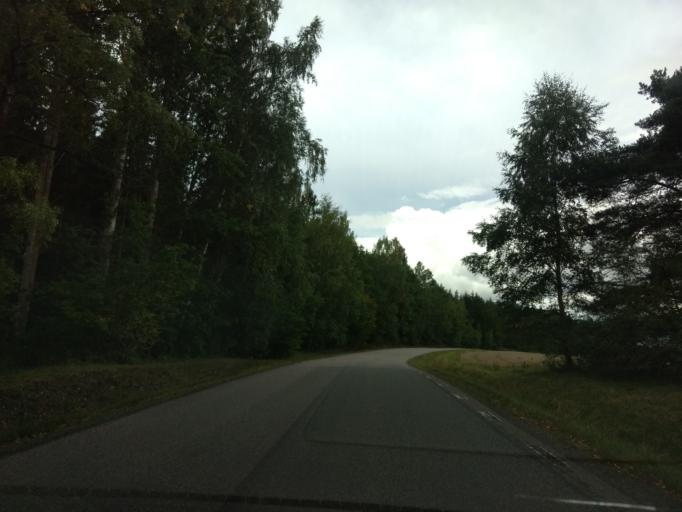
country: SE
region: Uppsala
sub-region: Habo Kommun
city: Balsta
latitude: 59.6819
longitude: 17.5333
